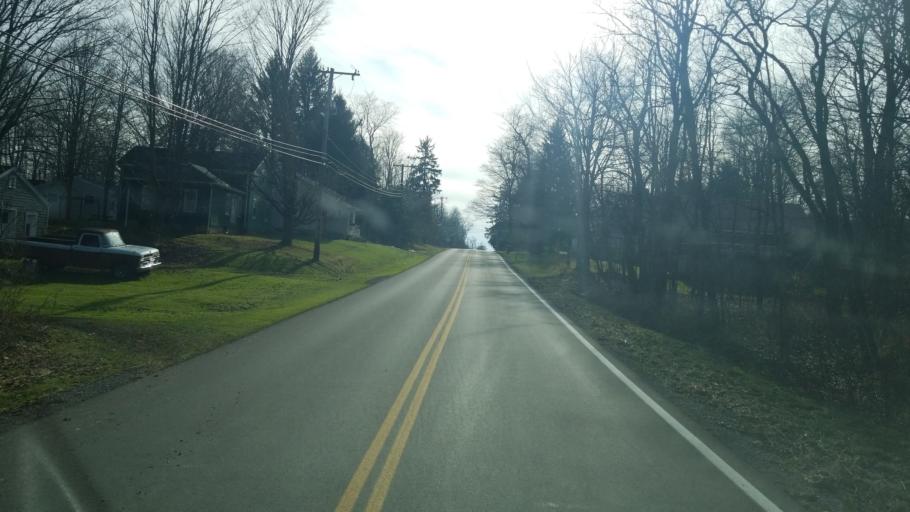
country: US
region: Ohio
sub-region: Ashtabula County
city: Roaming Shores
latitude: 41.6635
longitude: -80.9146
